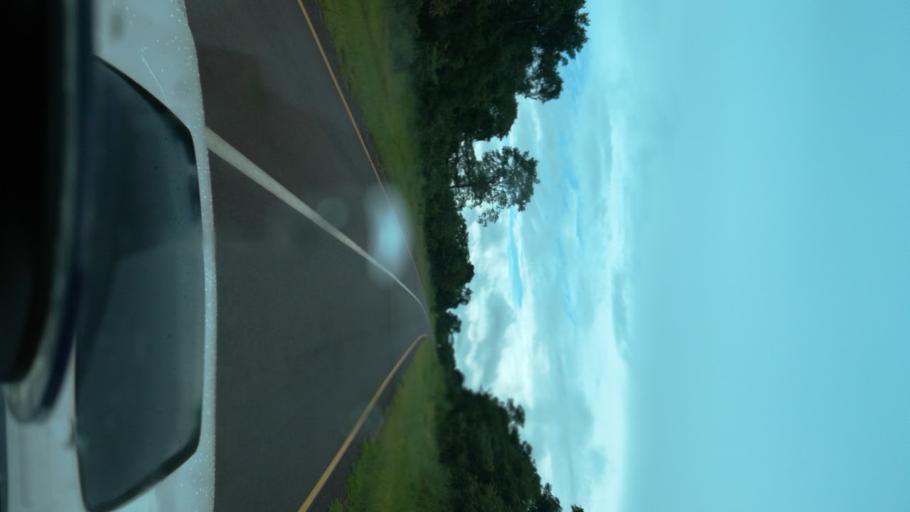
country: ZM
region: Luapula
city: Mwense
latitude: -10.8396
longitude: 28.2305
